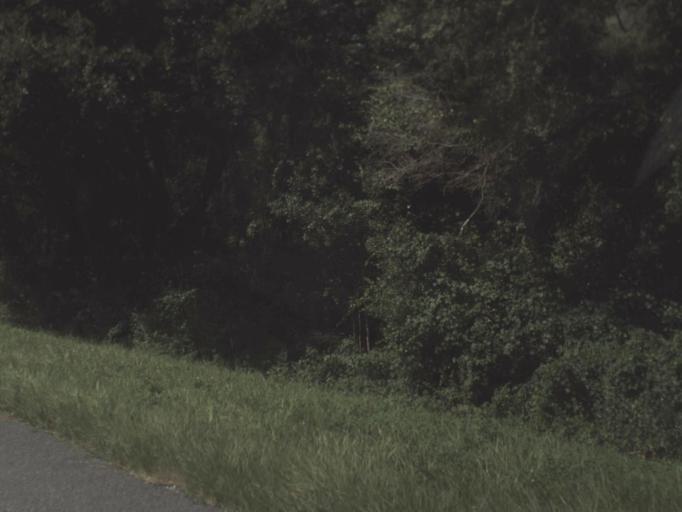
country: US
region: Florida
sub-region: Citrus County
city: Hernando
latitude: 28.9277
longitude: -82.3919
